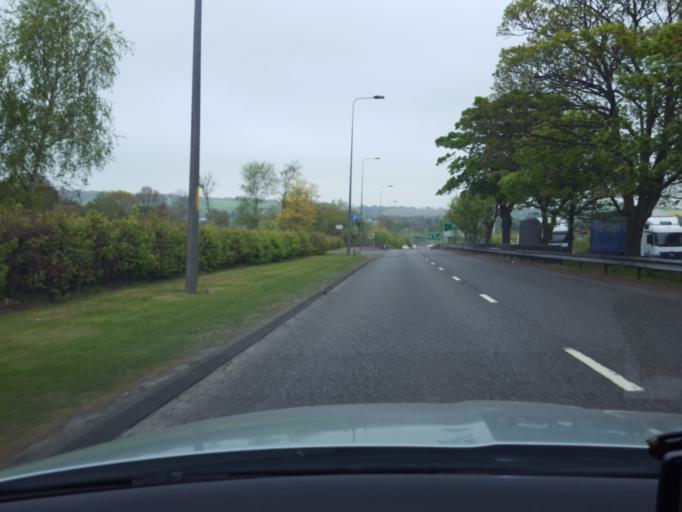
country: GB
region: Scotland
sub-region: Dundee City
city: Dundee
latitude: 56.4833
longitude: -2.9518
